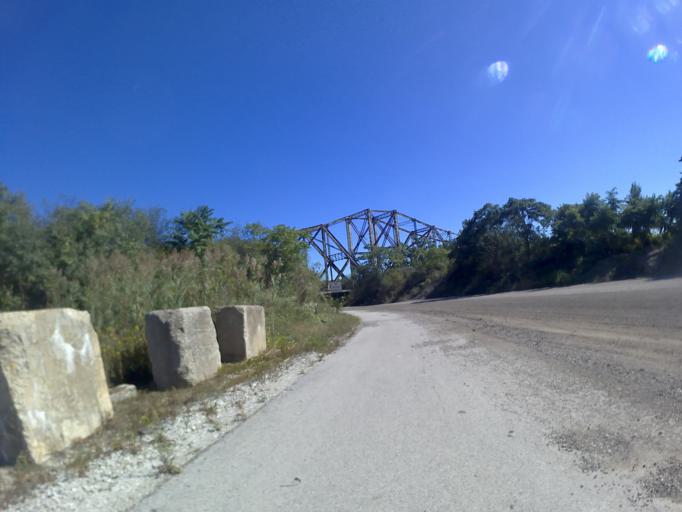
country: US
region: Illinois
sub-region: Cook County
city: Lemont
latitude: 41.6804
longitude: -88.0009
